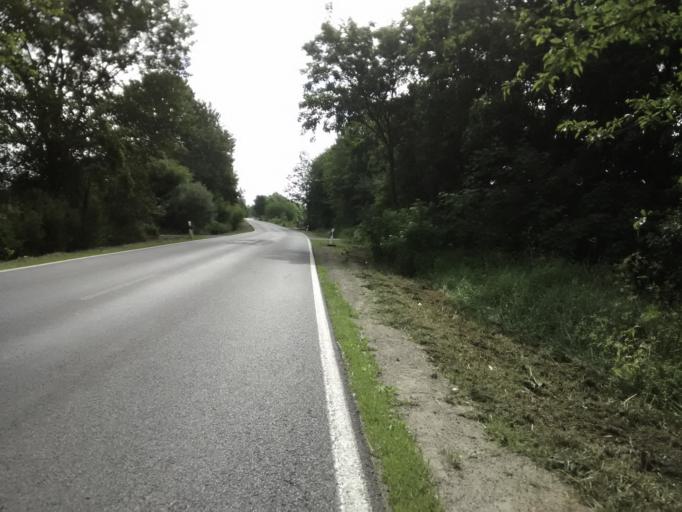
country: DE
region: Berlin
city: Blankenfelde
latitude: 52.6627
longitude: 13.4030
